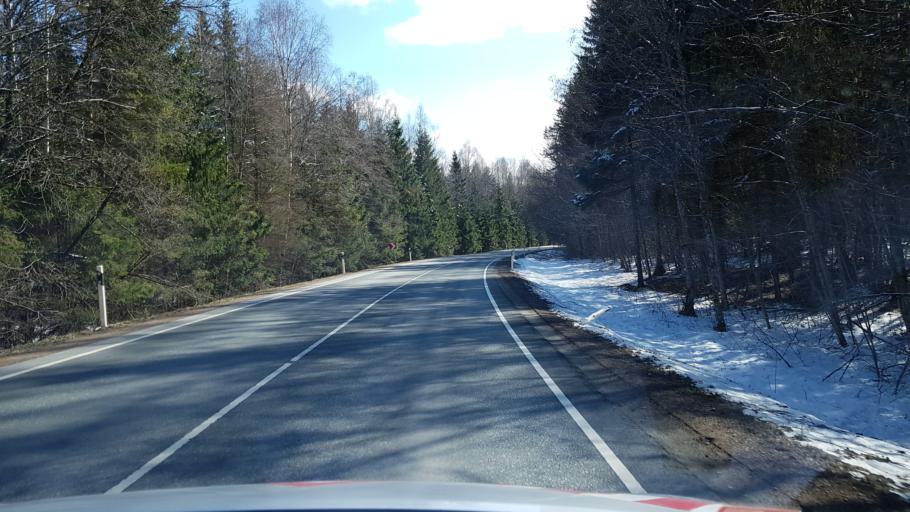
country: EE
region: Laeaene-Virumaa
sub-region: Tapa vald
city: Tapa
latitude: 59.4016
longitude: 26.0103
